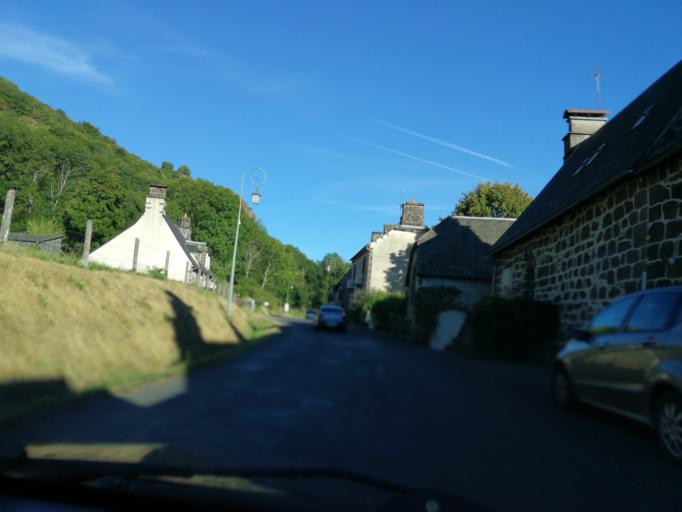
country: FR
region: Auvergne
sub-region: Departement du Cantal
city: Saint-Cernin
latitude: 45.1169
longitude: 2.4999
